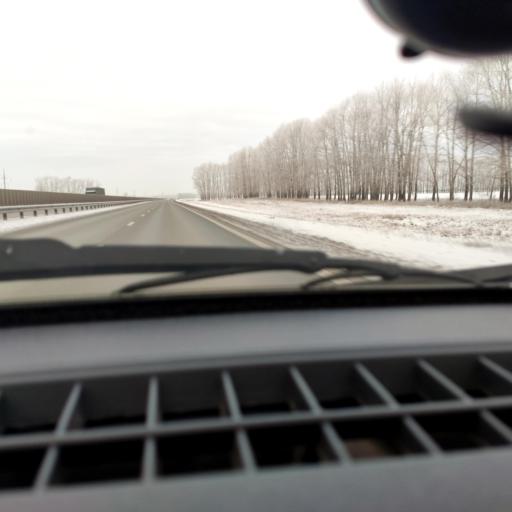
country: RU
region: Bashkortostan
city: Asanovo
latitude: 54.9931
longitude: 55.5103
